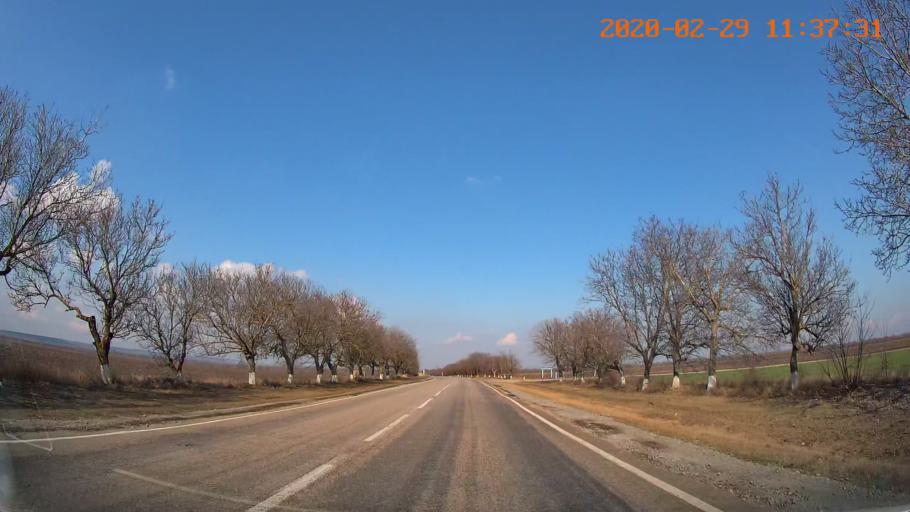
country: MD
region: Rezina
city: Saharna
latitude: 47.6127
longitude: 29.0455
